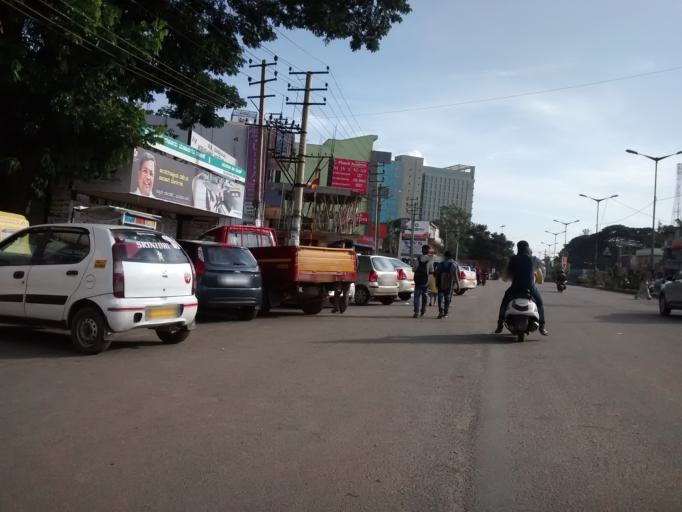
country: IN
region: Karnataka
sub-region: Bangalore Urban
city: Yelahanka
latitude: 13.0980
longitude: 77.5967
